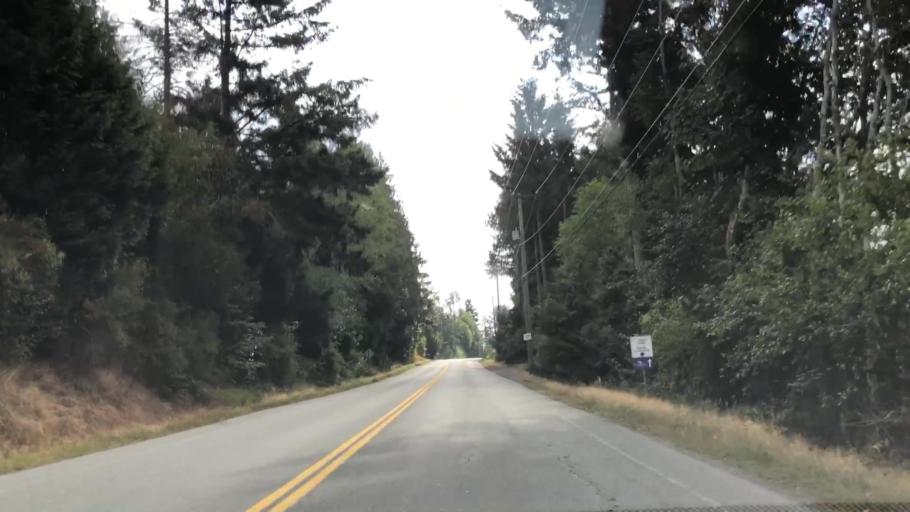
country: CA
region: British Columbia
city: North Saanich
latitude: 48.6879
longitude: -123.5680
